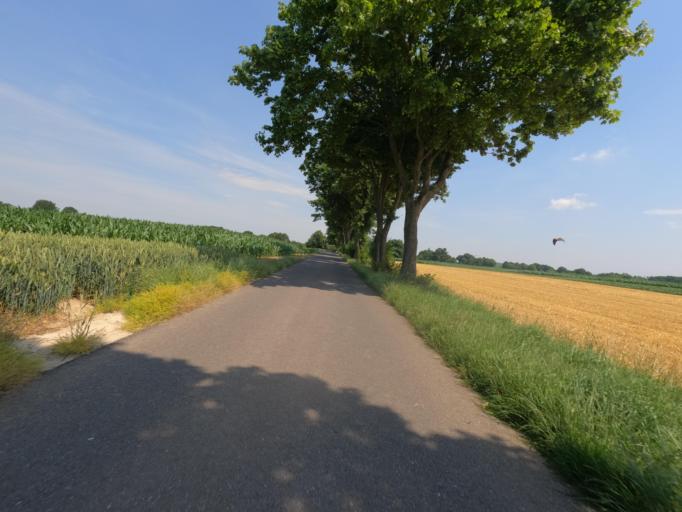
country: DE
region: North Rhine-Westphalia
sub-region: Regierungsbezirk Koln
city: Ubach-Palenberg
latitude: 50.9392
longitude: 6.0855
